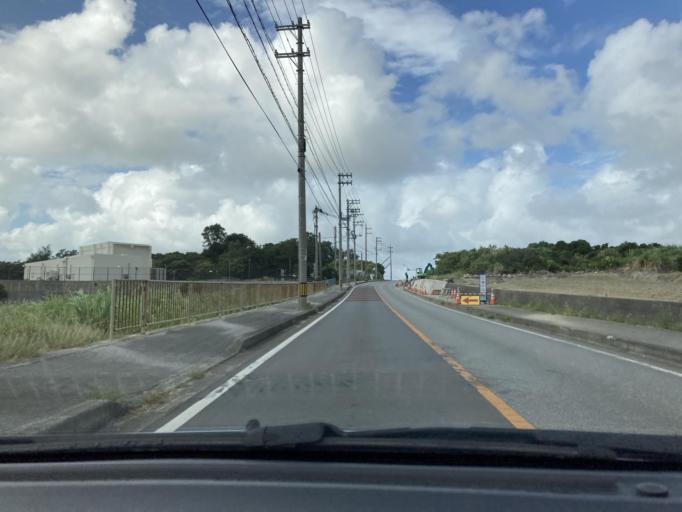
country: JP
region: Okinawa
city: Itoman
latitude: 26.1078
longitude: 127.6945
